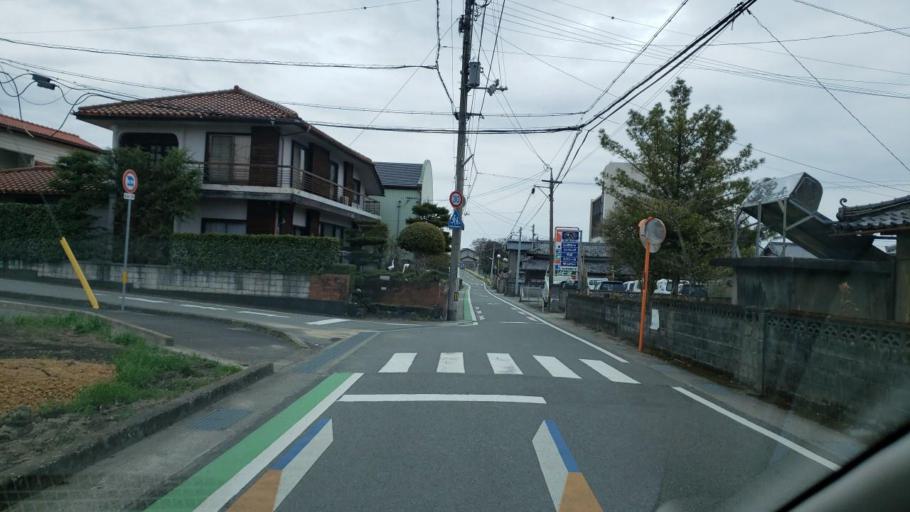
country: JP
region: Tokushima
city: Kamojimacho-jogejima
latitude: 34.0861
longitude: 134.2864
